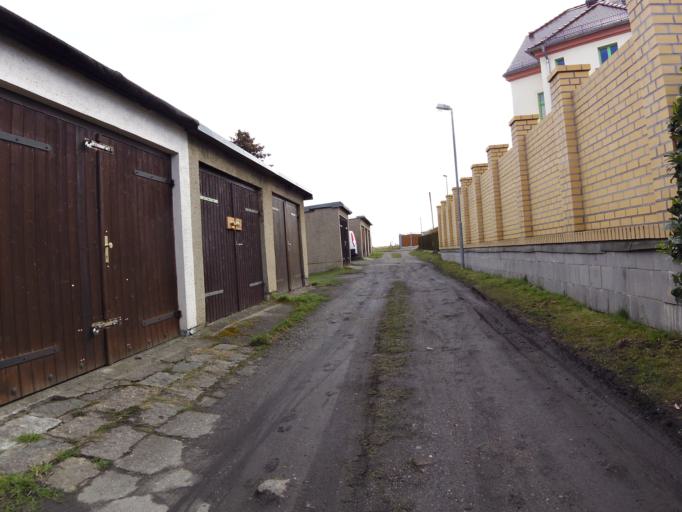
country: DE
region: Saxony
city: Taucha
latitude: 51.3328
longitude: 12.4783
